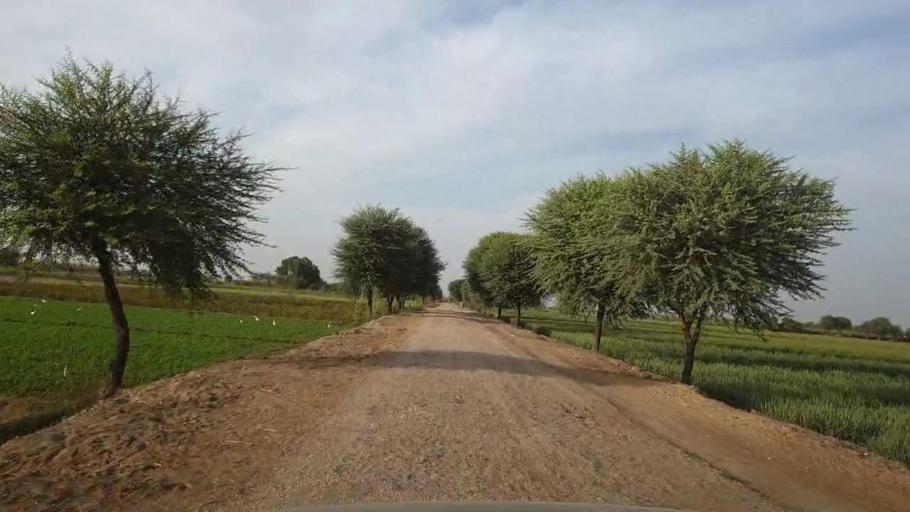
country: PK
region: Sindh
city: Kunri
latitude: 25.2214
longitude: 69.5021
